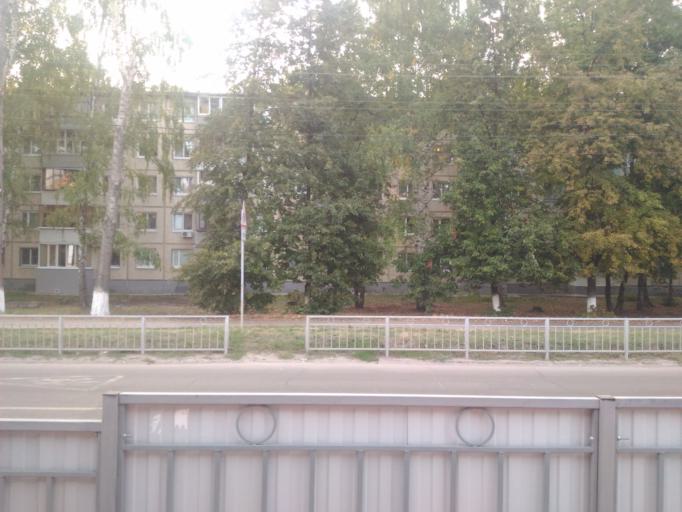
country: RU
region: Ulyanovsk
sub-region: Ulyanovskiy Rayon
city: Ulyanovsk
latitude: 54.2824
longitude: 48.2985
